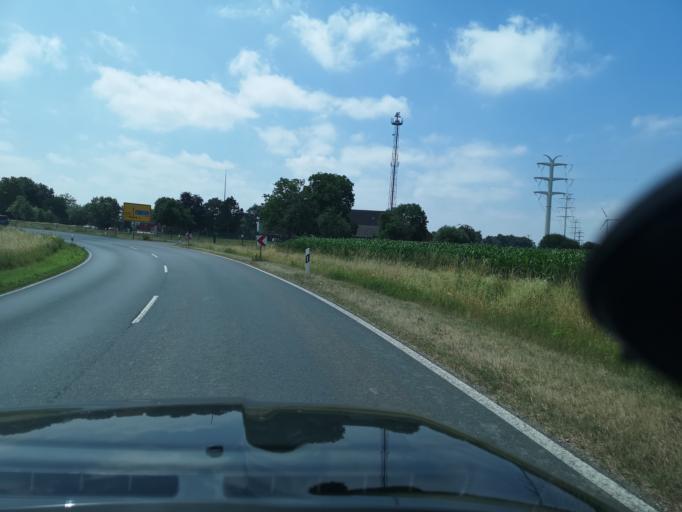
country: DE
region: North Rhine-Westphalia
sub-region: Regierungsbezirk Munster
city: Isselburg
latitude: 51.8214
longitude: 6.4434
